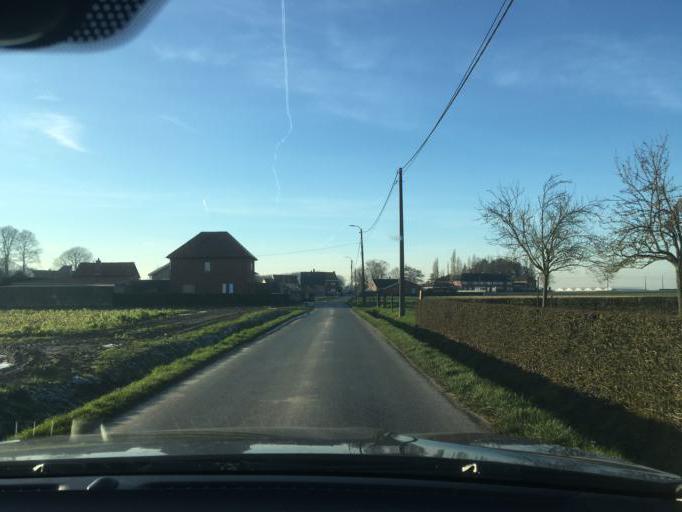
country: BE
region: Flanders
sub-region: Provincie West-Vlaanderen
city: Pittem
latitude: 50.9646
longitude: 3.2474
